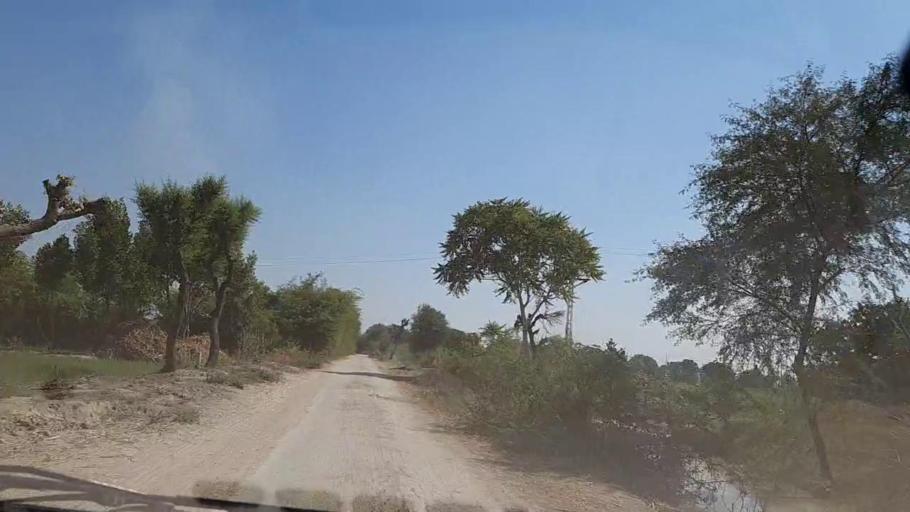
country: PK
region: Sindh
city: Mirpur Khas
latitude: 25.4304
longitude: 69.0217
